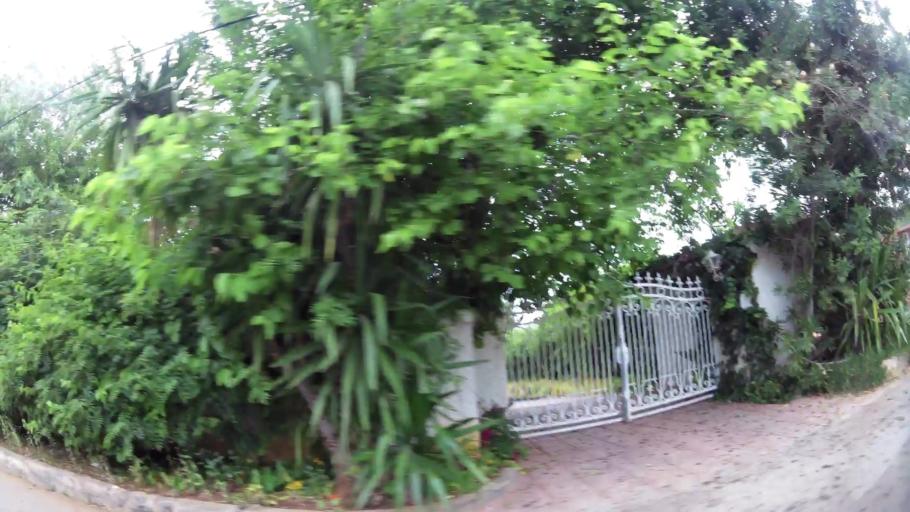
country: MA
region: Rabat-Sale-Zemmour-Zaer
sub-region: Rabat
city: Rabat
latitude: 33.9654
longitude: -6.8189
